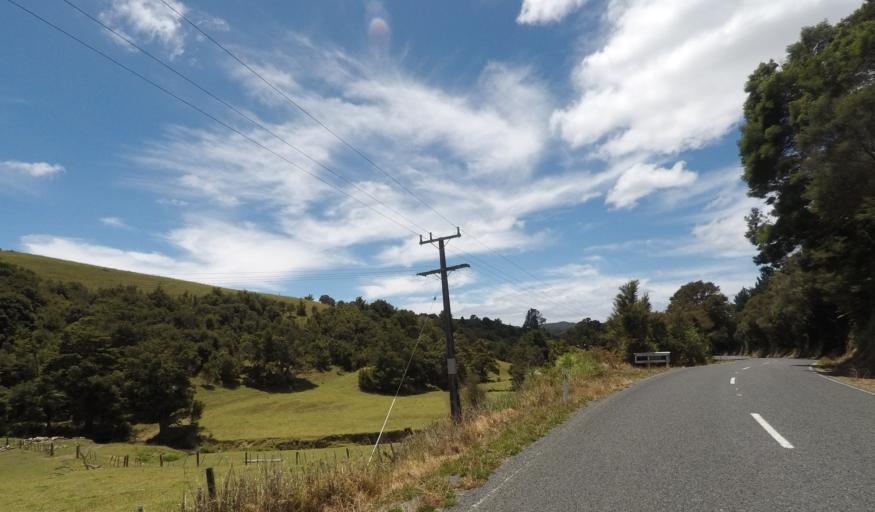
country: NZ
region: Northland
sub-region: Whangarei
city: Ngunguru
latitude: -35.5068
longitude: 174.4015
